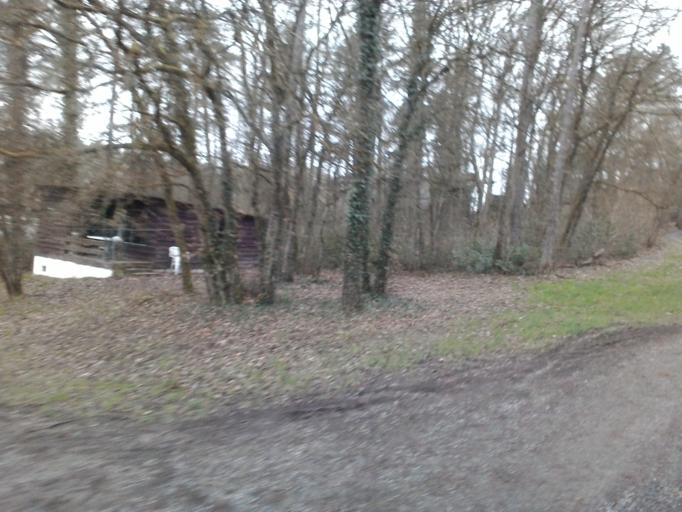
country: BE
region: Wallonia
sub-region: Province du Luxembourg
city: Wellin
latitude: 50.1127
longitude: 5.1353
